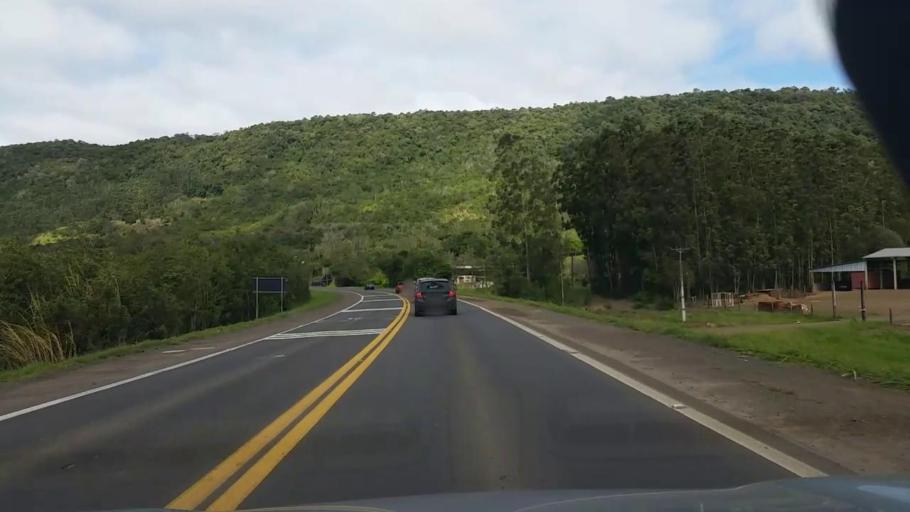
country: BR
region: Rio Grande do Sul
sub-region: Arroio Do Meio
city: Arroio do Meio
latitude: -29.3290
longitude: -52.1017
